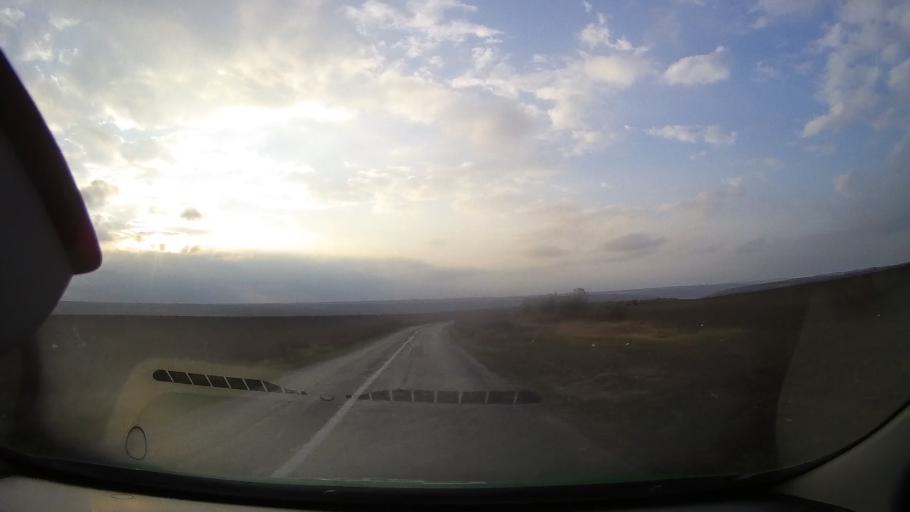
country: RO
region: Constanta
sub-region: Comuna Adamclisi
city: Adamclisi
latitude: 44.0165
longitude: 27.8960
